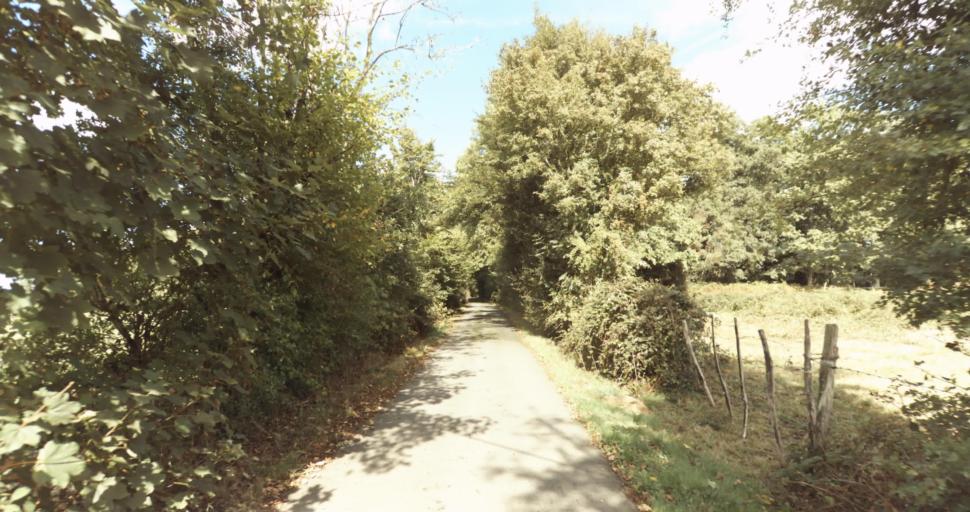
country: FR
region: Lower Normandy
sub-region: Departement de l'Orne
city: Vimoutiers
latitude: 48.9334
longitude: 0.2603
